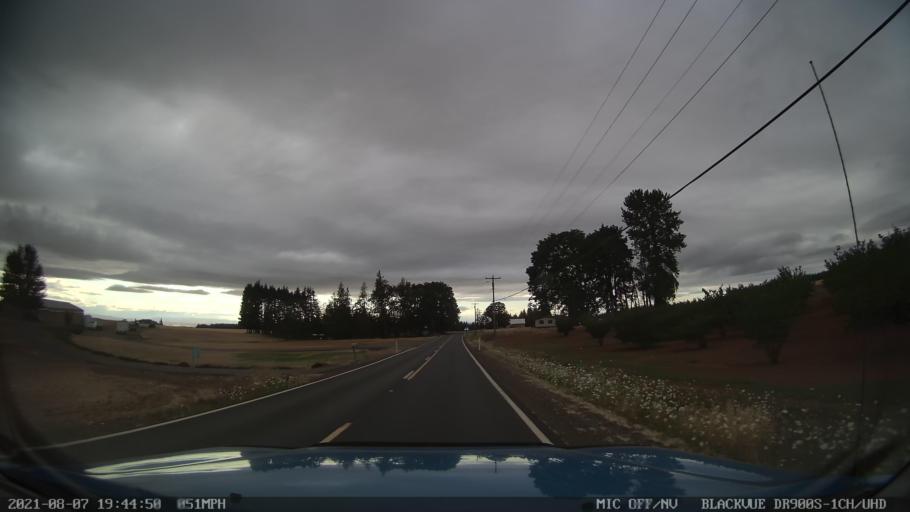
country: US
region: Oregon
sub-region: Marion County
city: Silverton
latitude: 44.9429
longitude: -122.6885
